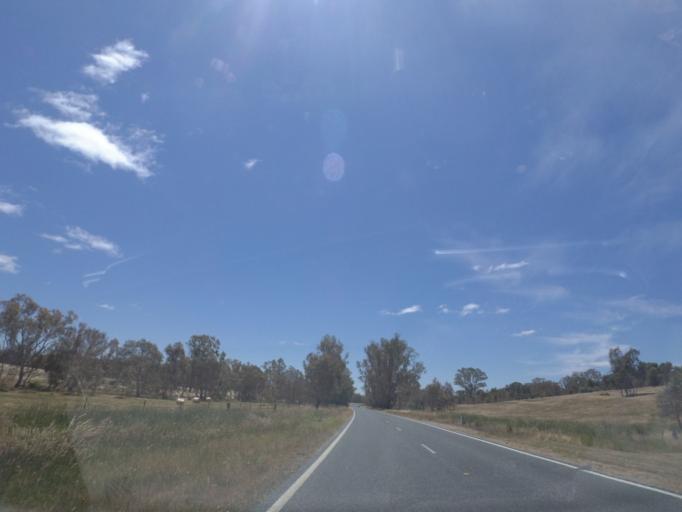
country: AU
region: Victoria
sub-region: Mount Alexander
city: Castlemaine
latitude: -37.1775
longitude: 144.1474
